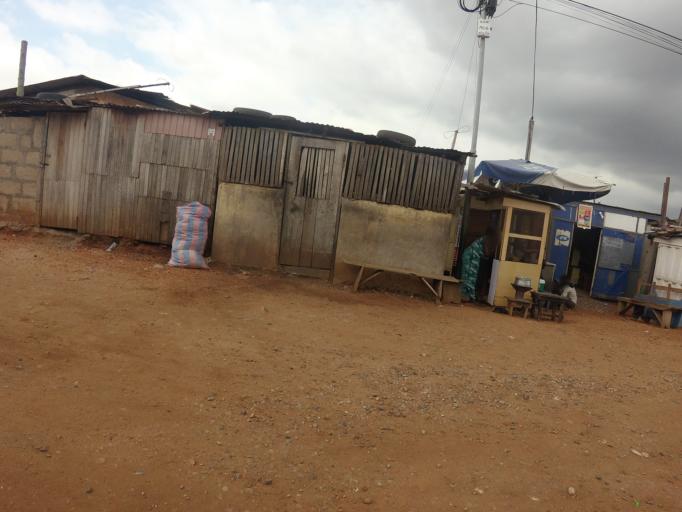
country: GH
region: Greater Accra
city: Accra
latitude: 5.5874
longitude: -0.2035
